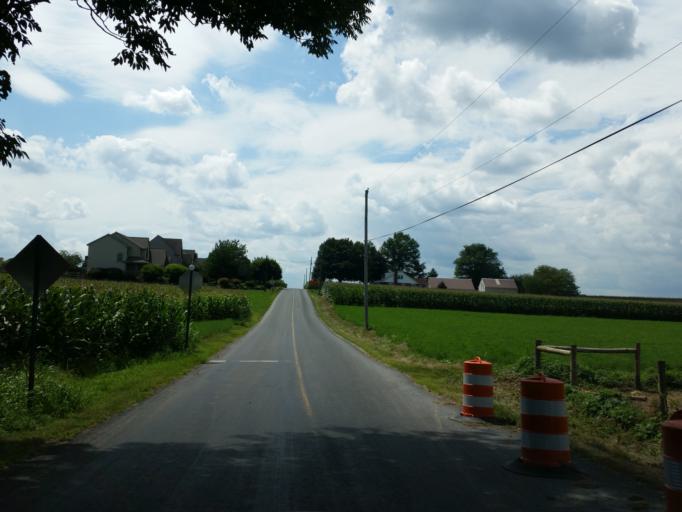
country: US
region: Pennsylvania
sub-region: Lancaster County
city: Strasburg
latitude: 39.9722
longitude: -76.1927
